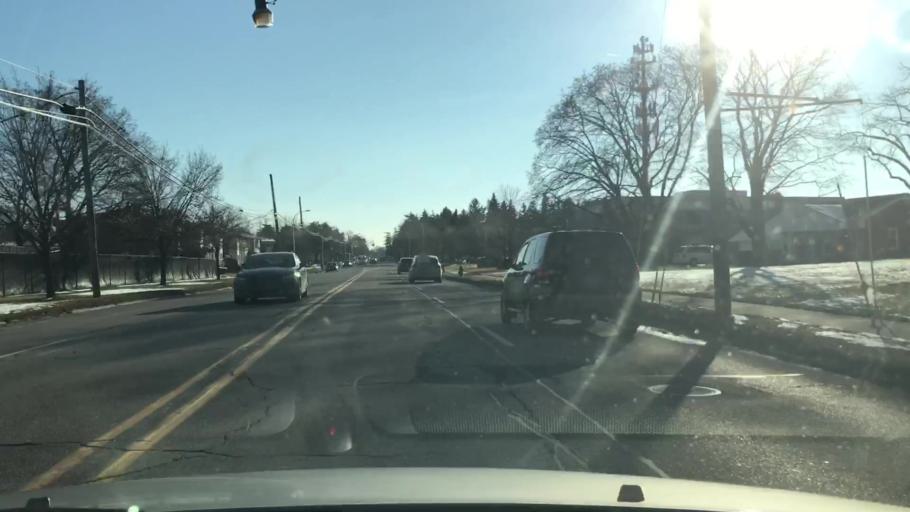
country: US
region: Michigan
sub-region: Oakland County
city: Royal Oak
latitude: 42.5067
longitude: -83.1426
